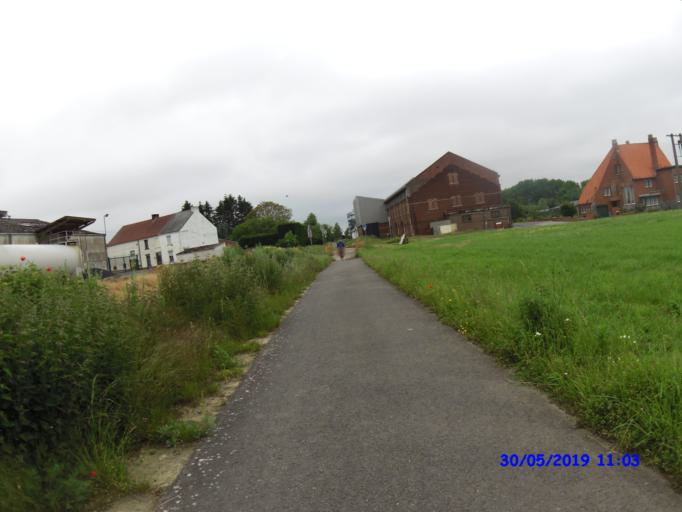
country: BE
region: Wallonia
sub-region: Province du Hainaut
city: Thuin
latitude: 50.2801
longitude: 4.3164
